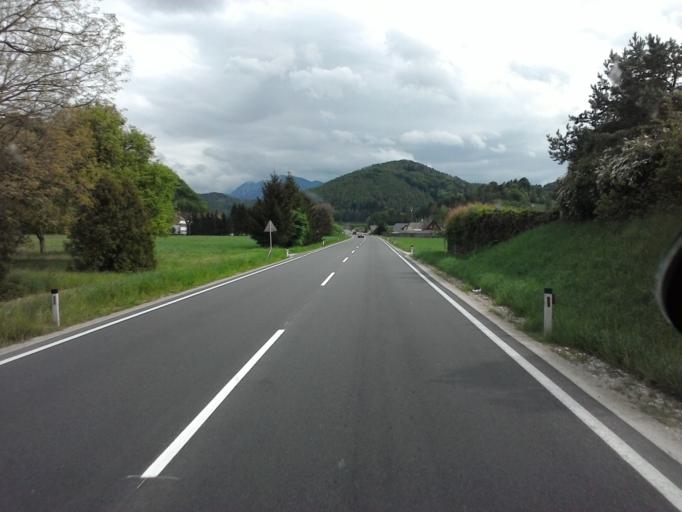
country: AT
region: Upper Austria
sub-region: Politischer Bezirk Kirchdorf an der Krems
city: Micheldorf in Oberoesterreich
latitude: 47.8745
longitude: 14.1308
